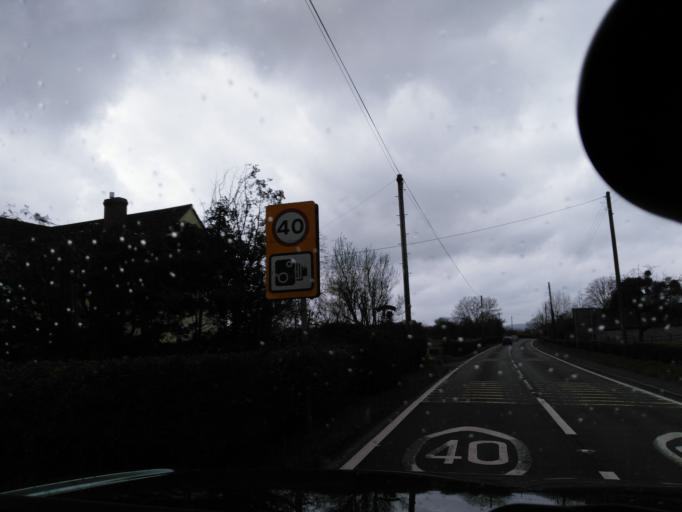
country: GB
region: England
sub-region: Somerset
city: Wells
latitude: 51.1426
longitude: -2.6521
